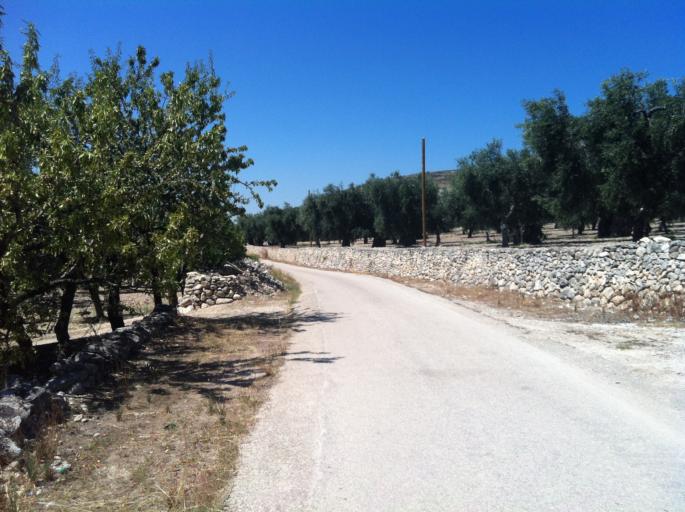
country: IT
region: Apulia
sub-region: Provincia di Foggia
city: Monte Sant'Angelo
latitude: 41.6659
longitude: 15.9470
